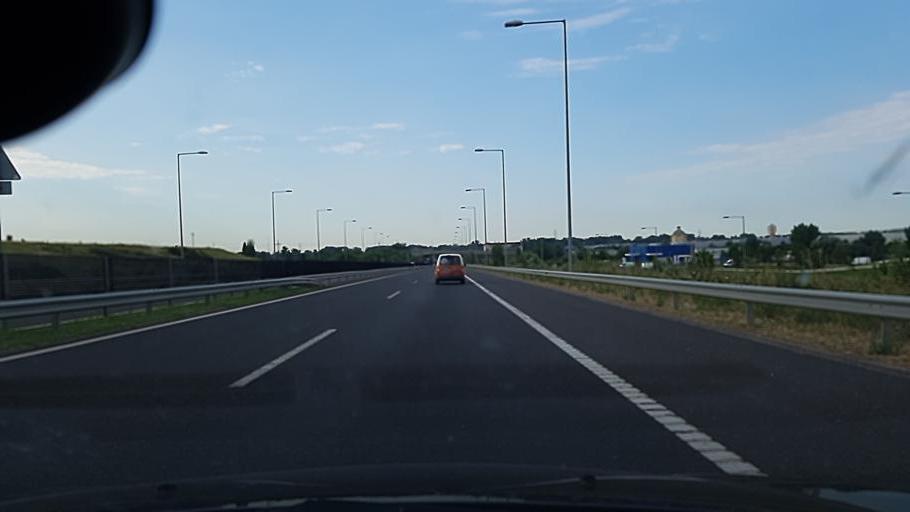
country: HU
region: Pest
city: Diosd
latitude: 47.3944
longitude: 18.9694
